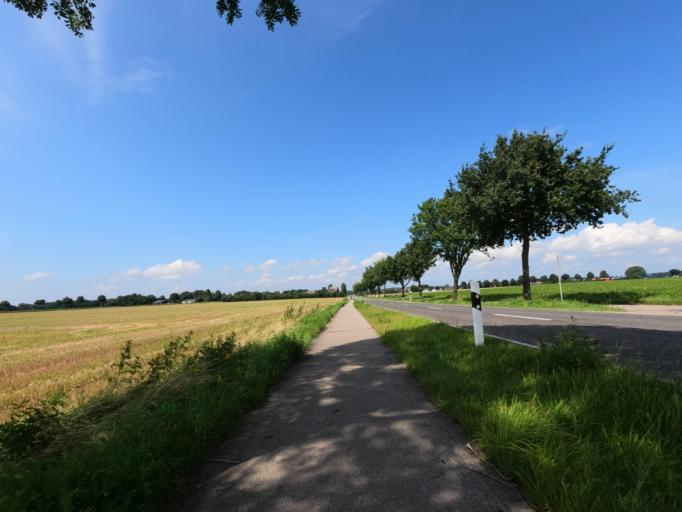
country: DE
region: North Rhine-Westphalia
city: Geilenkirchen
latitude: 50.9551
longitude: 6.1363
